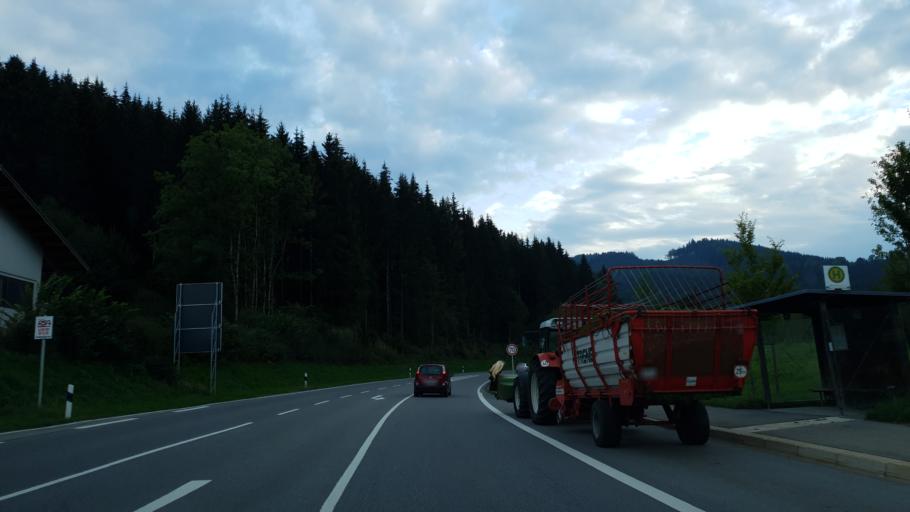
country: DE
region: Bavaria
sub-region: Swabia
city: Maierhofen
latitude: 47.6559
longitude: 10.0890
